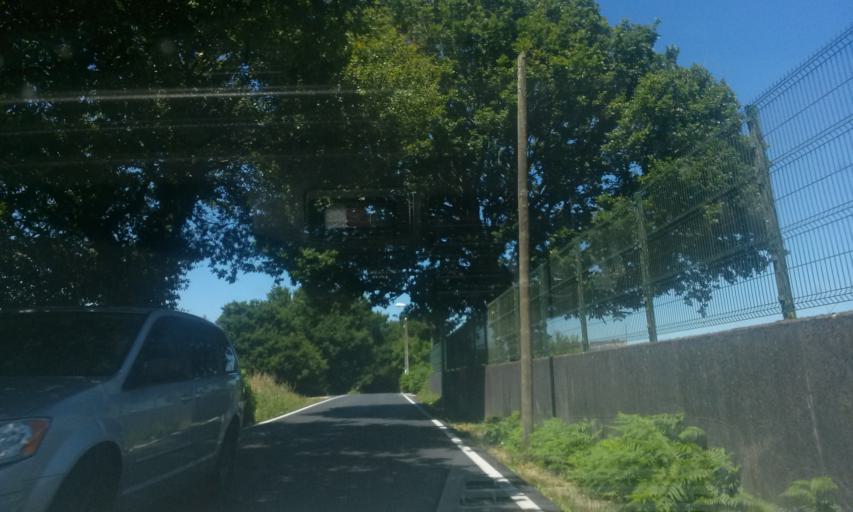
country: ES
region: Galicia
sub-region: Provincia de Lugo
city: Lugo
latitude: 43.0241
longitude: -7.5752
